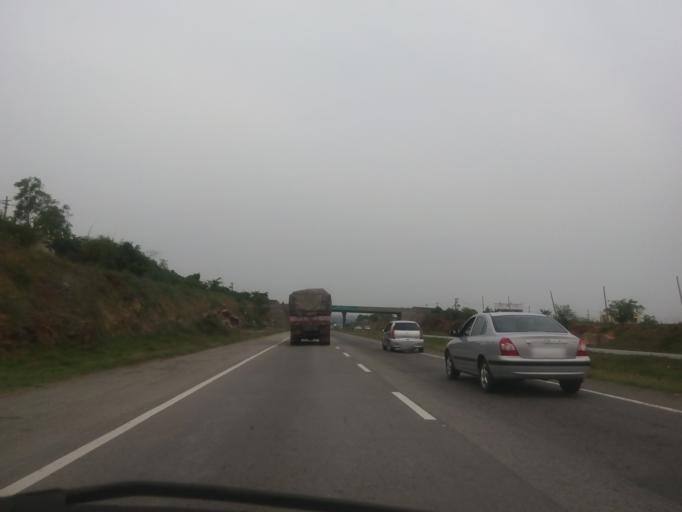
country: IN
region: Karnataka
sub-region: Bangalore Urban
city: Bangalore
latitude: 12.9639
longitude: 77.4715
